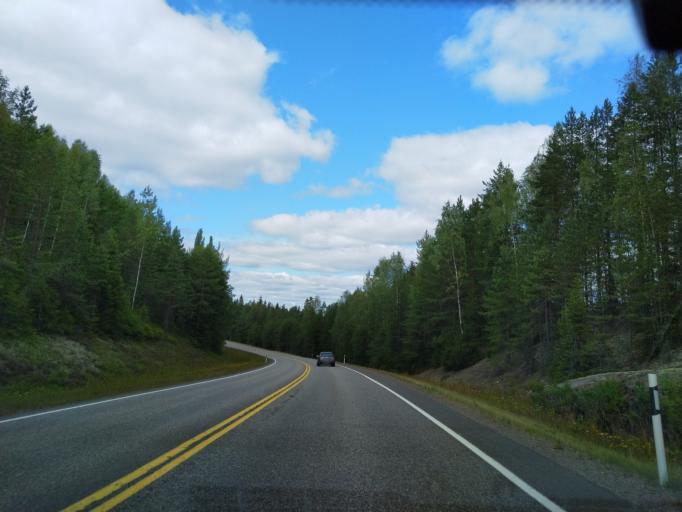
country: FI
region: Haeme
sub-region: Riihimaeki
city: Loppi
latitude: 60.7420
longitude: 24.3614
